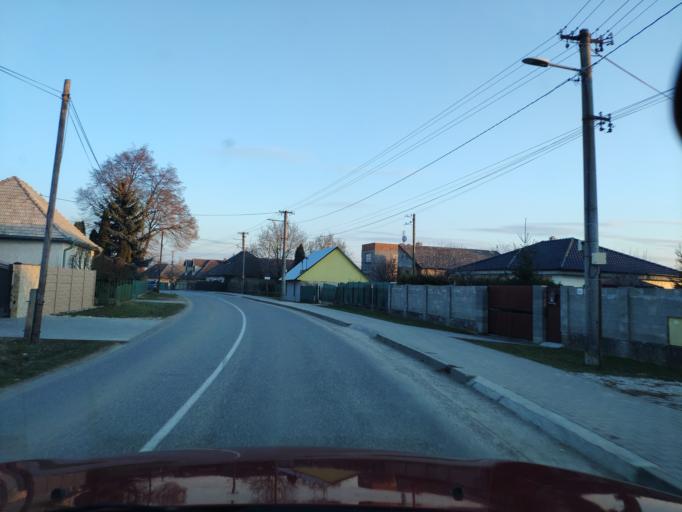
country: SK
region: Nitriansky
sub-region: Okres Nitra
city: Nitra
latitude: 48.2122
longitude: 18.0591
